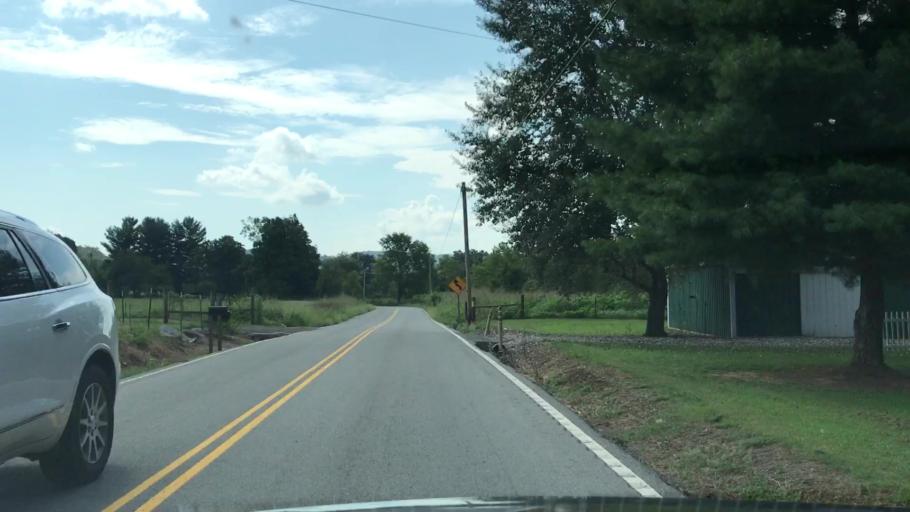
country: US
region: Tennessee
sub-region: Trousdale County
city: Hartsville
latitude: 36.4759
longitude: -86.1830
